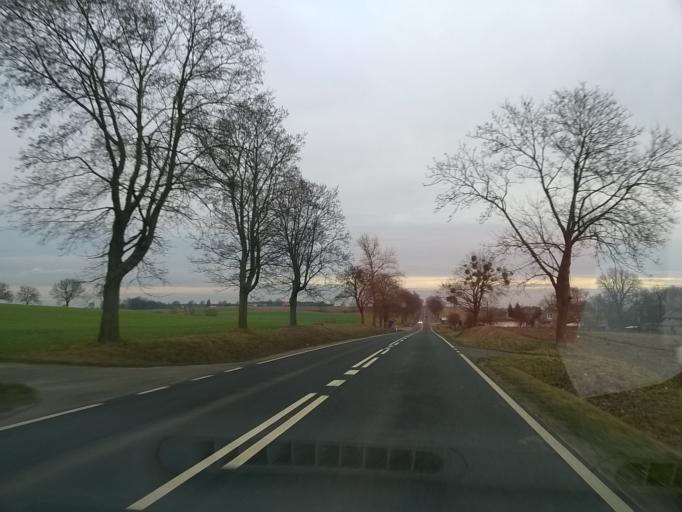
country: PL
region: Kujawsko-Pomorskie
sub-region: Powiat nakielski
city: Naklo nad Notecia
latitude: 53.0899
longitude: 17.6631
